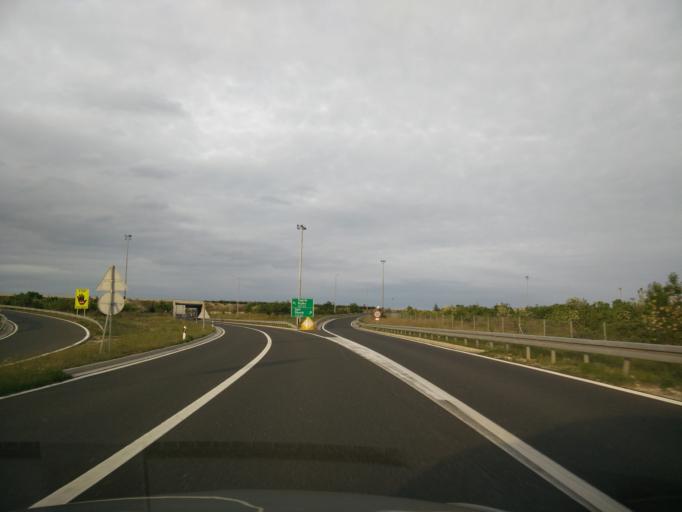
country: HR
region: Zadarska
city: Galovac
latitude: 44.1134
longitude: 15.4418
